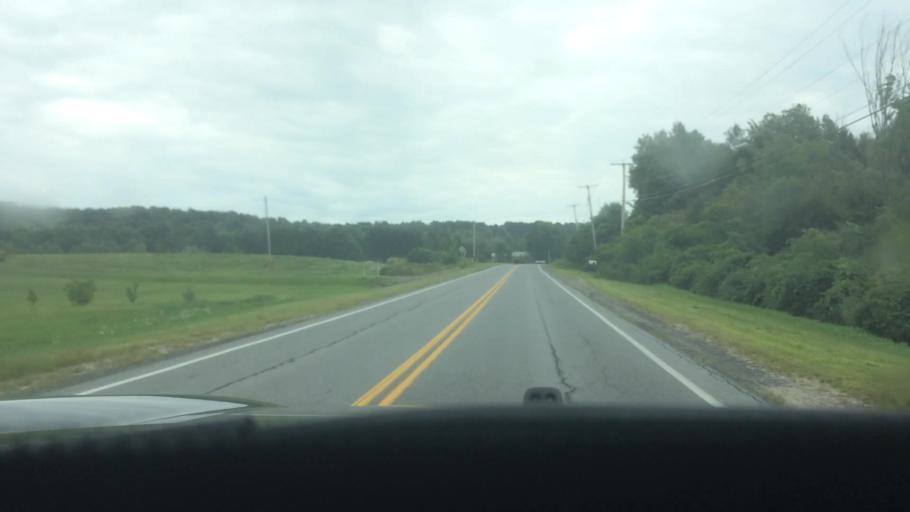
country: US
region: New York
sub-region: St. Lawrence County
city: Canton
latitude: 44.5483
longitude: -75.1046
